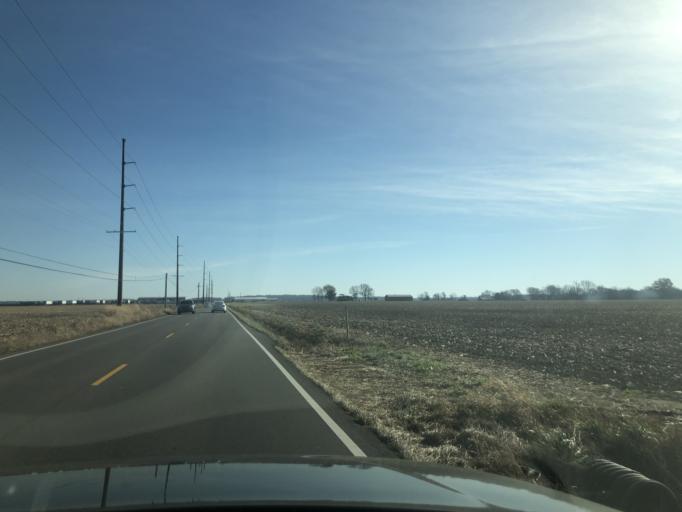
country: US
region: Indiana
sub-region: Warrick County
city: Newburgh
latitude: 37.9912
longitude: -87.4530
